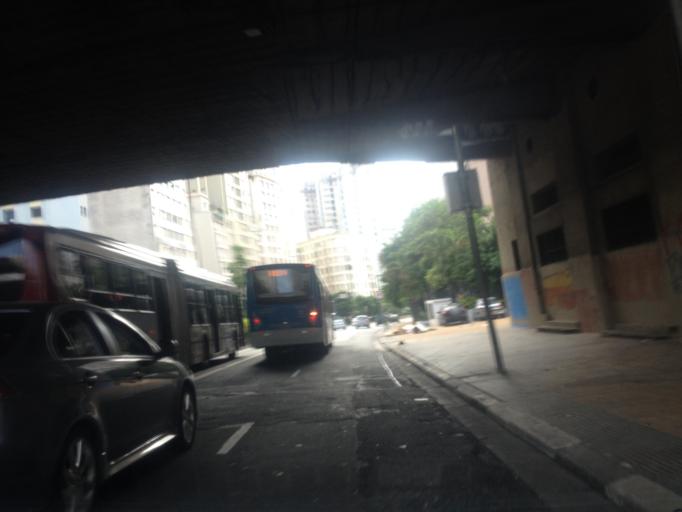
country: BR
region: Sao Paulo
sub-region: Sao Paulo
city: Sao Paulo
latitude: -23.5498
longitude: -46.6425
